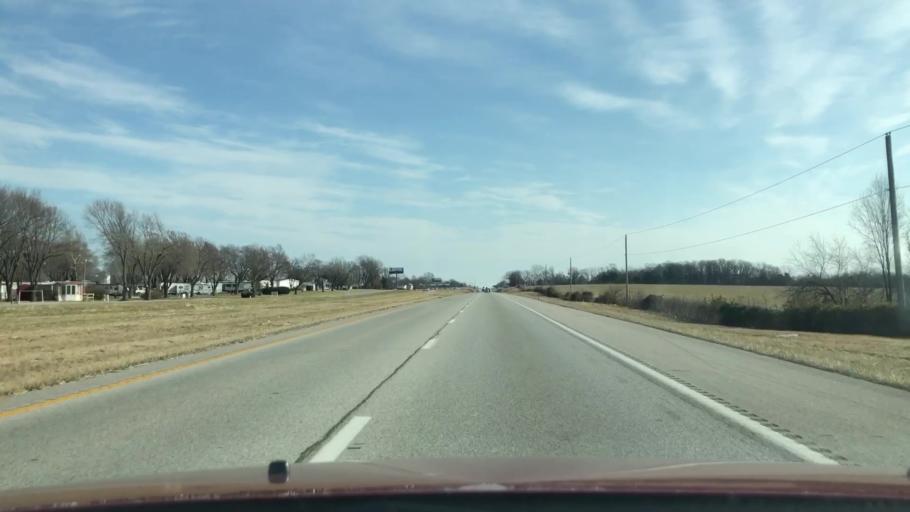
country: US
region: Missouri
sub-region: Webster County
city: Rogersville
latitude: 37.1189
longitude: -93.1319
